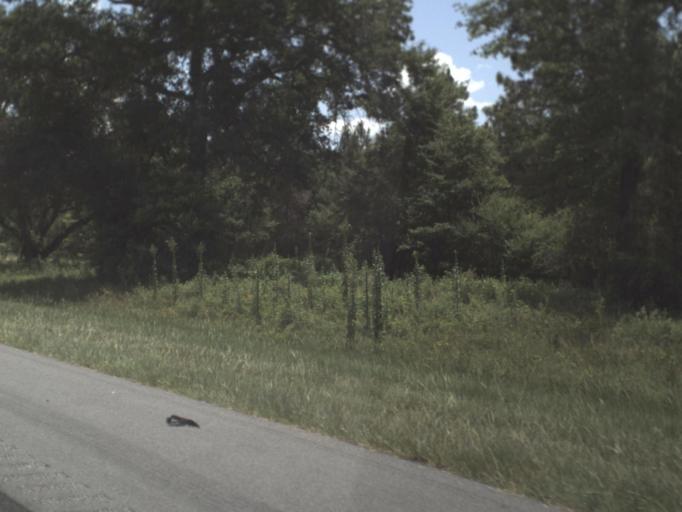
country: US
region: Florida
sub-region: Madison County
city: Madison
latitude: 30.3814
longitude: -83.3052
